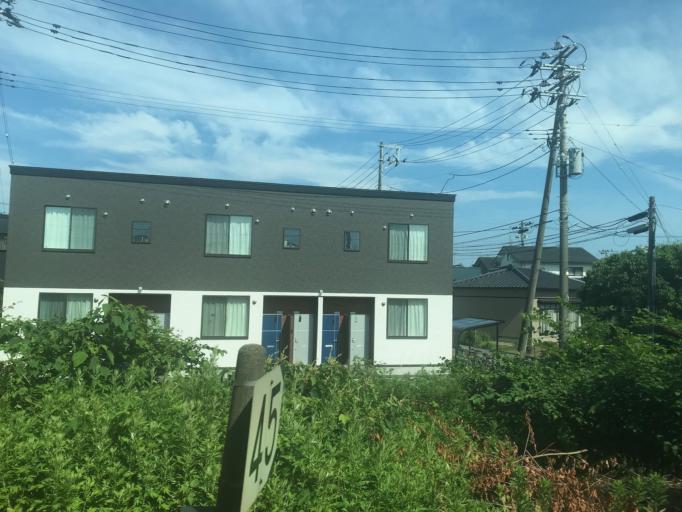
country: JP
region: Niigata
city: Suibara
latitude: 37.9218
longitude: 139.2179
